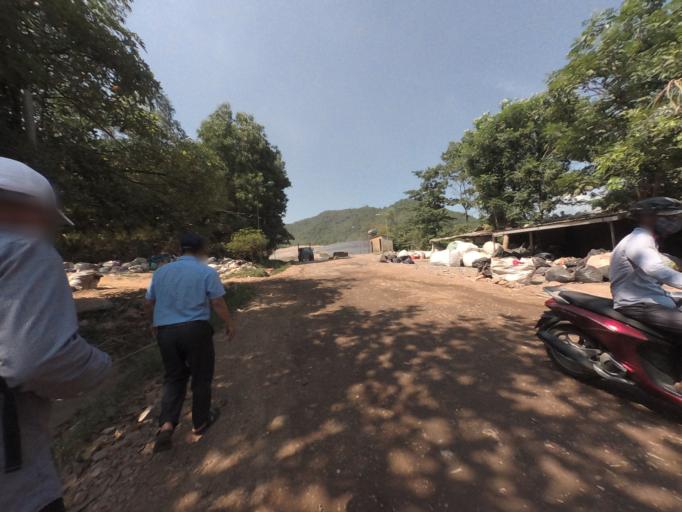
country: VN
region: Da Nang
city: Lien Chieu
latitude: 16.0451
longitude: 108.1423
